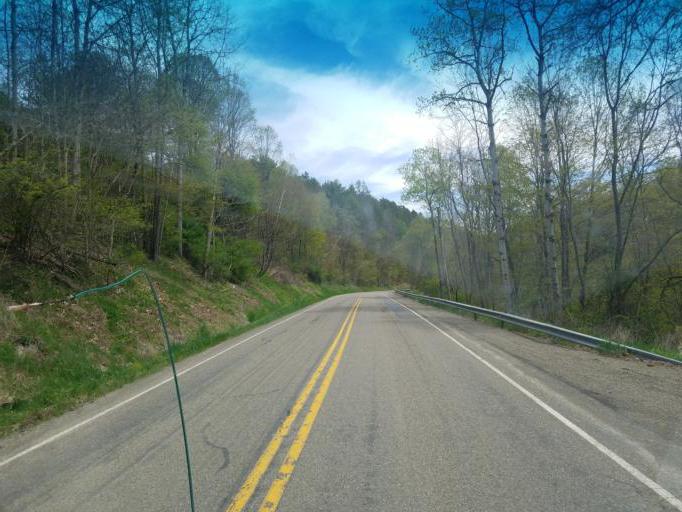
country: US
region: Pennsylvania
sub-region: Tioga County
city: Wellsboro
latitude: 41.7275
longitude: -77.4150
